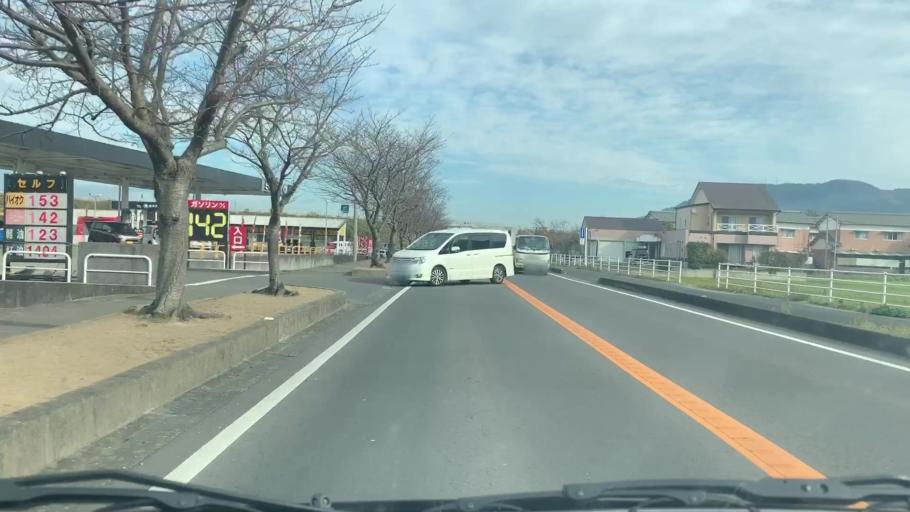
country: JP
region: Saga Prefecture
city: Karatsu
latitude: 33.4116
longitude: 129.9923
